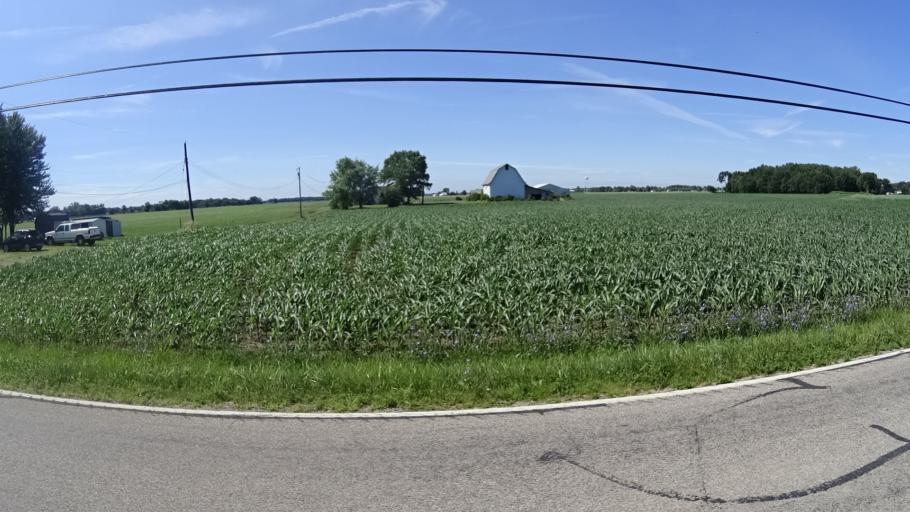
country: US
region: Ohio
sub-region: Ottawa County
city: Port Clinton
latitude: 41.4312
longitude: -82.8923
